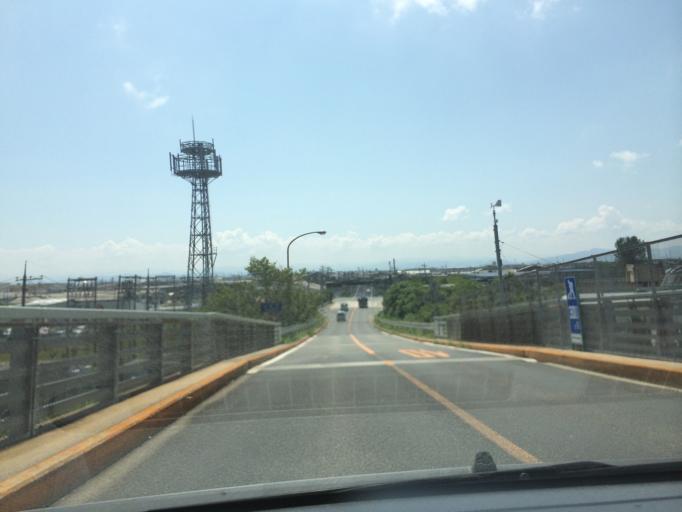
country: JP
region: Shimane
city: Sakaiminato
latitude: 35.5450
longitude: 133.2459
